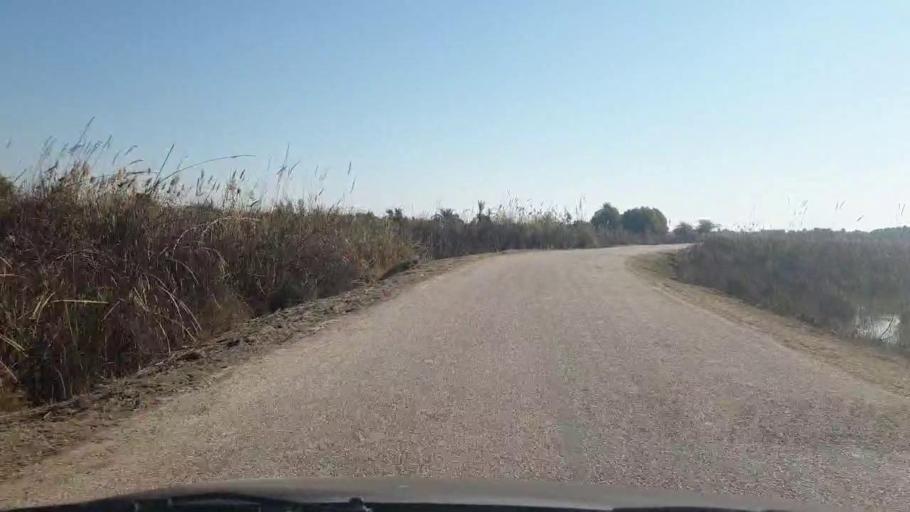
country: PK
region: Sindh
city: Bozdar
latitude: 27.1593
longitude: 68.6478
